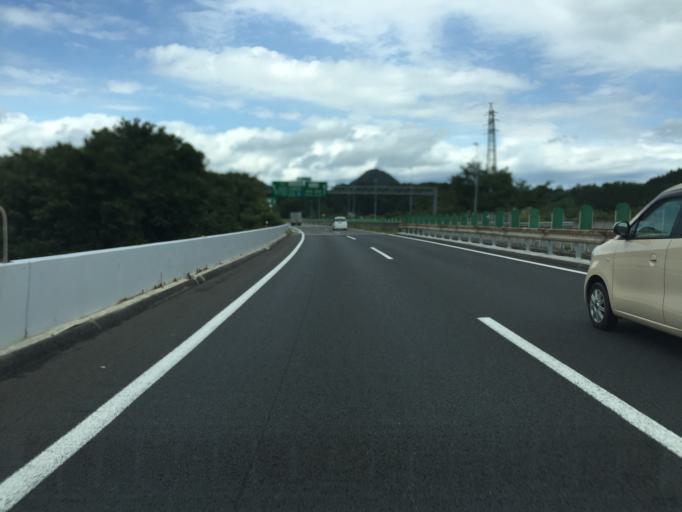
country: JP
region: Miyagi
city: Sendai
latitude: 38.2117
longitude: 140.8047
